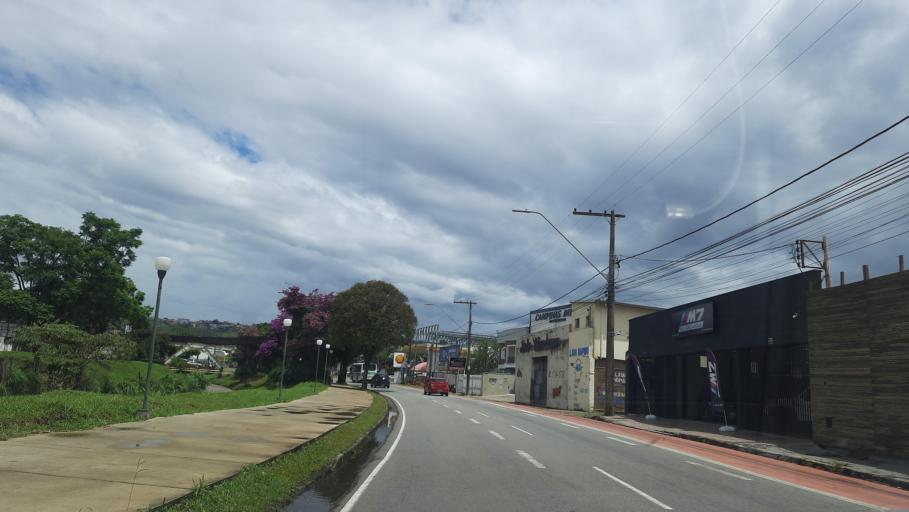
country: BR
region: Minas Gerais
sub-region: Pocos De Caldas
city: Pocos de Caldas
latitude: -21.7837
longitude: -46.5974
